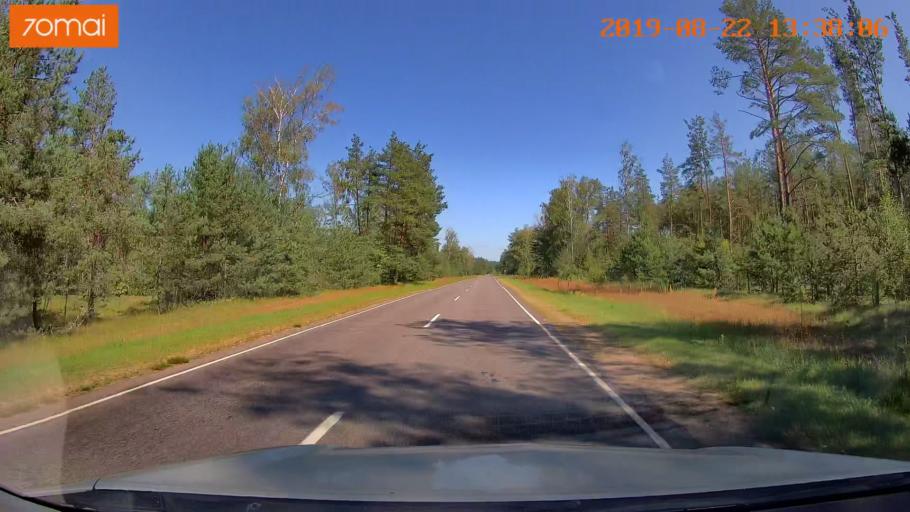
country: BY
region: Minsk
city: Staryya Darohi
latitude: 53.2209
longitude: 28.3143
